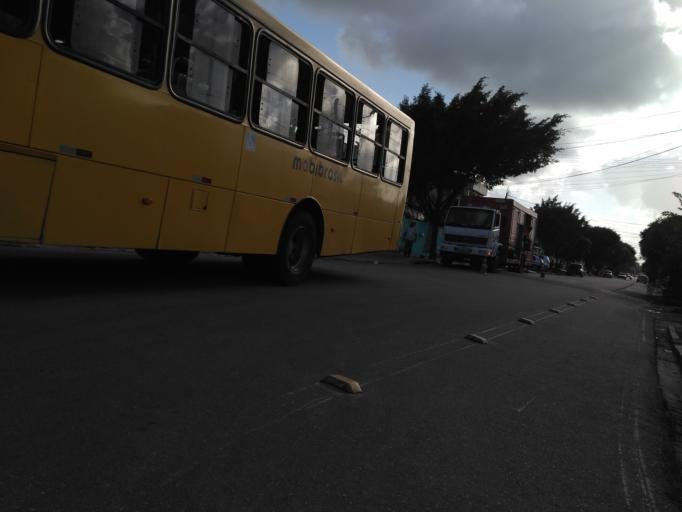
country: BR
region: Pernambuco
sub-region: Recife
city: Recife
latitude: -8.0606
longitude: -34.9426
